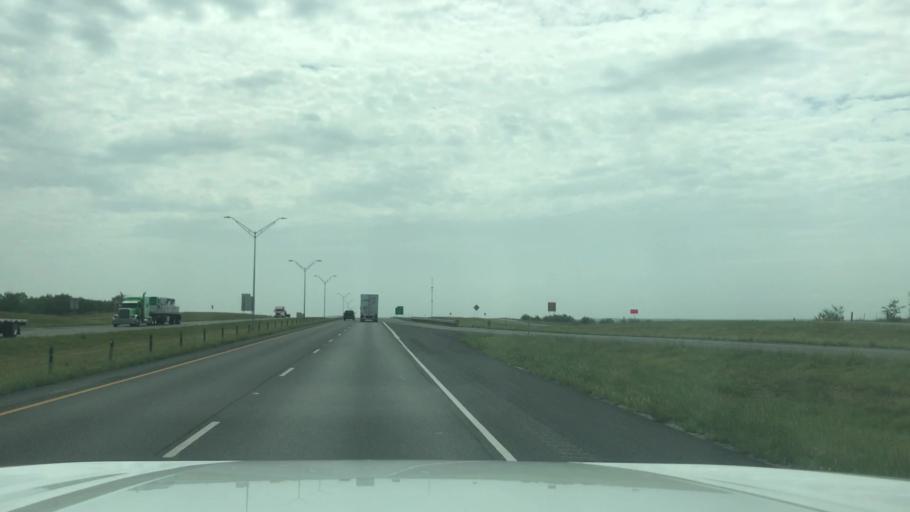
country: US
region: Texas
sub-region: Callahan County
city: Baird
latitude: 32.4007
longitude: -99.3820
